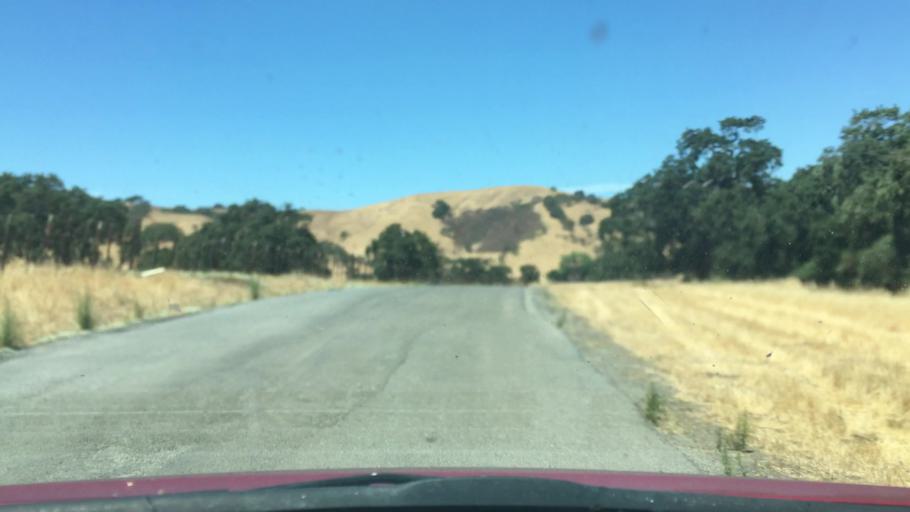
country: US
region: California
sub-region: Santa Clara County
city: Morgan Hill
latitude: 37.1556
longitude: -121.7121
